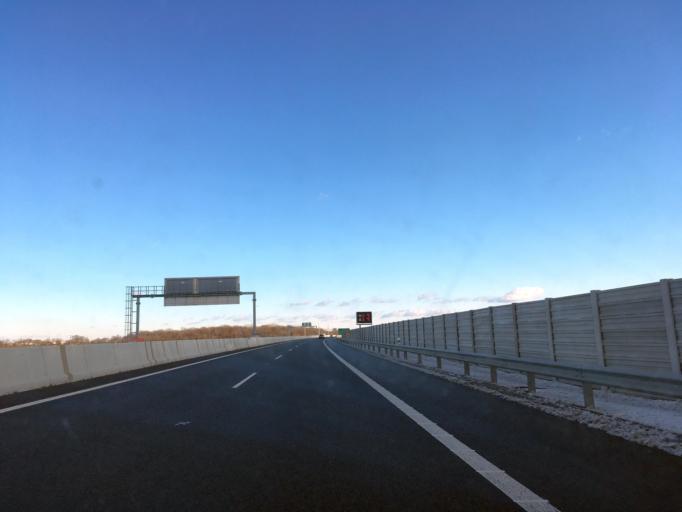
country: SK
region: Bratislavsky
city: Dunajska Luzna
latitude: 48.0869
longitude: 17.2105
